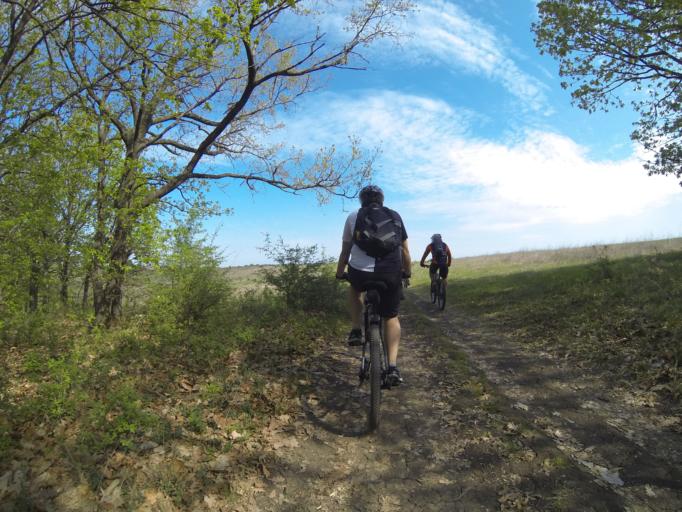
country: RO
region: Dolj
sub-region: Comuna Bradesti
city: Bradesti
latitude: 44.5259
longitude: 23.6162
